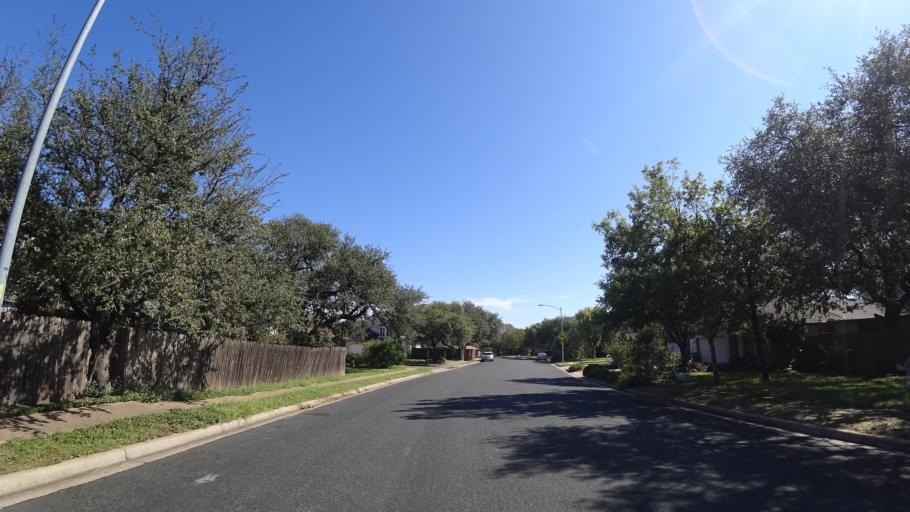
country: US
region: Texas
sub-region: Travis County
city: Shady Hollow
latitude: 30.2142
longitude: -97.8749
